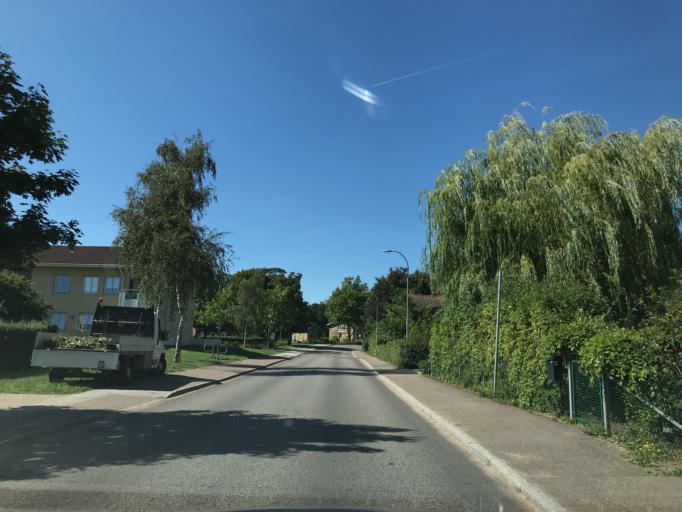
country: SE
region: Skane
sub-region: Tomelilla Kommun
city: Tomelilla
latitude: 55.6530
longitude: 13.8938
